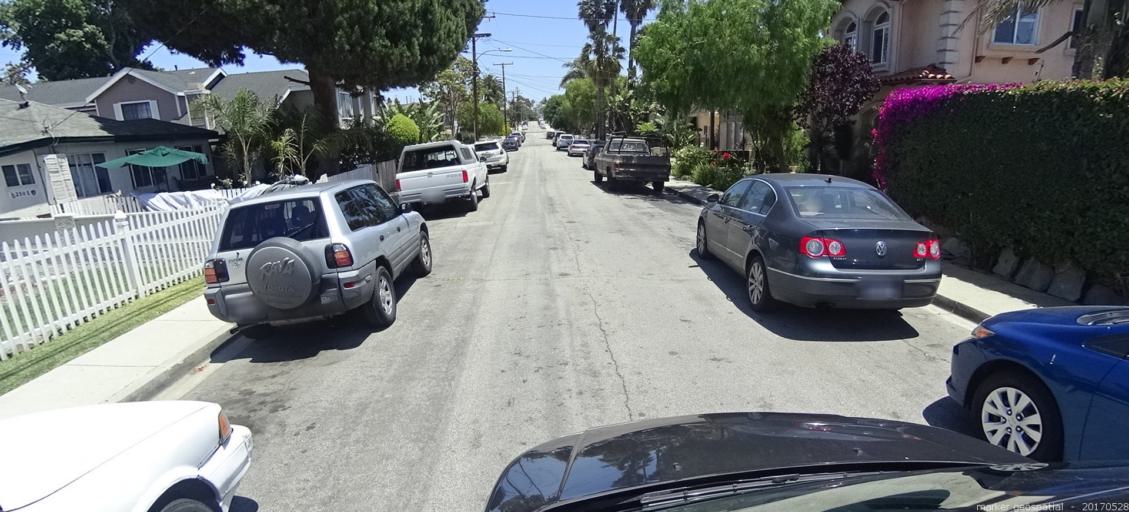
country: US
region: California
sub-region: Los Angeles County
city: Lawndale
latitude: 33.8681
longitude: -118.3662
